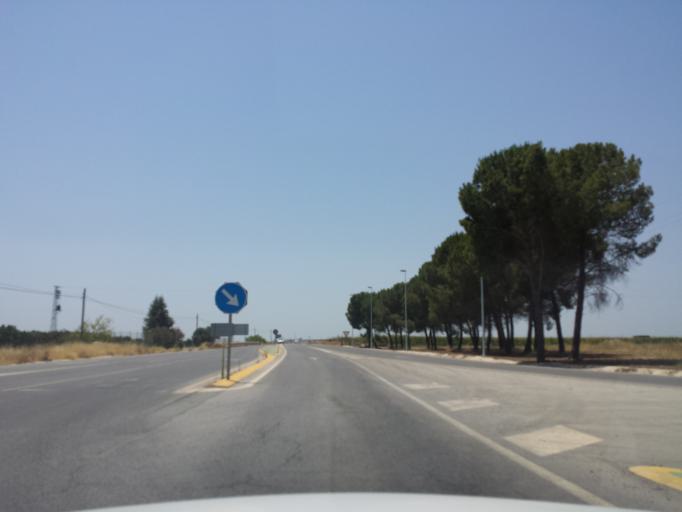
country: ES
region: Andalusia
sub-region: Provincia de Sevilla
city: Acala del Rio
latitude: 37.5430
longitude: -5.9444
